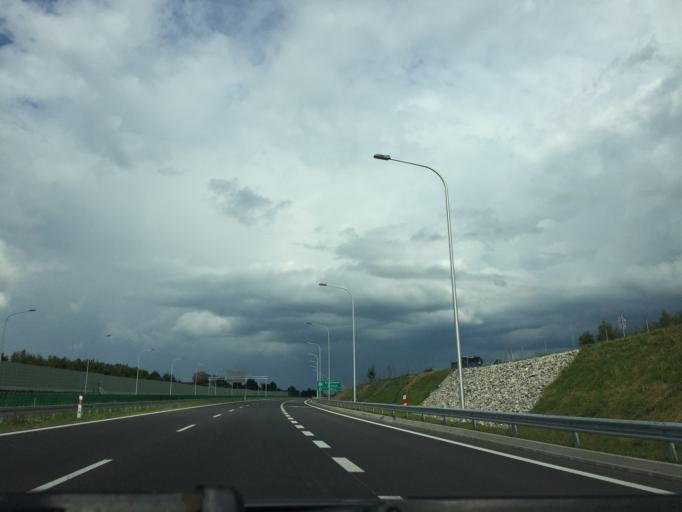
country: PL
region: Masovian Voivodeship
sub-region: Powiat szydlowiecki
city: Szydlowiec
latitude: 51.2397
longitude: 20.8767
